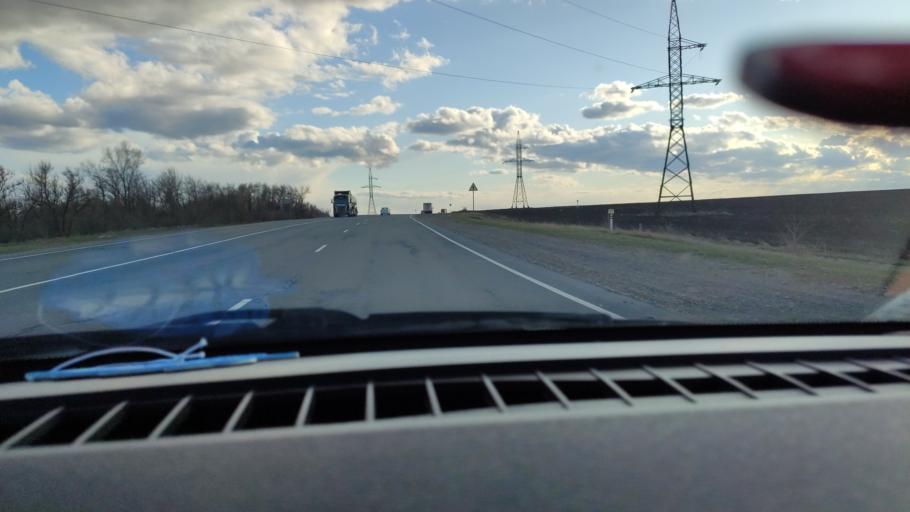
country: RU
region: Saratov
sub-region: Saratovskiy Rayon
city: Saratov
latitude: 51.7455
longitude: 46.0522
